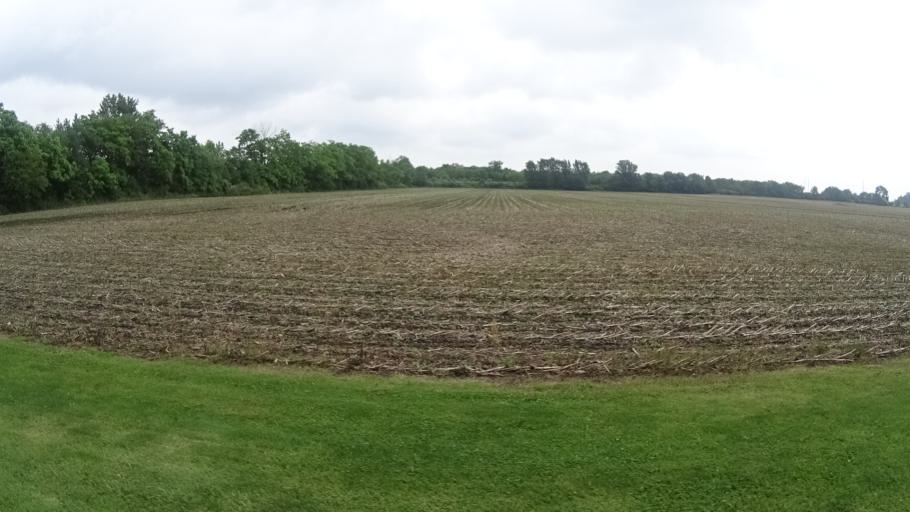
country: US
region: Ohio
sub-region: Huron County
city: Bellevue
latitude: 41.3581
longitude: -82.7731
